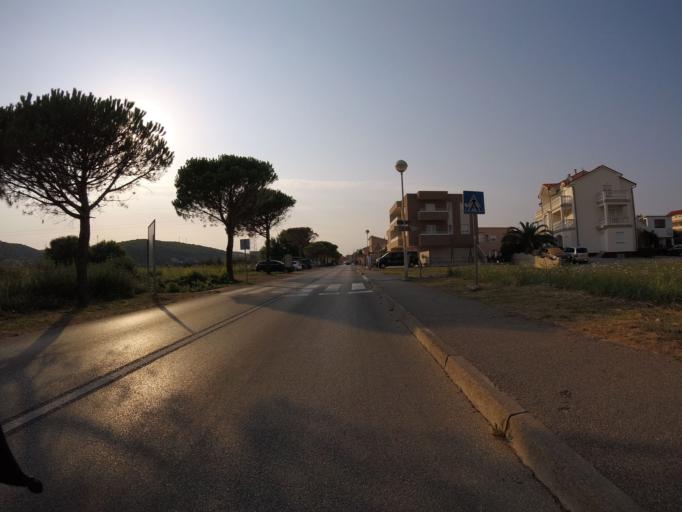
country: HR
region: Primorsko-Goranska
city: Lopar
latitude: 44.8283
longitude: 14.7340
